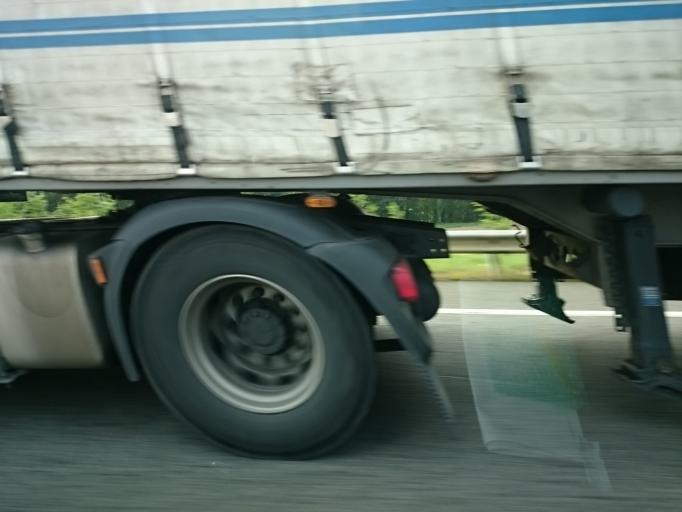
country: FR
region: Brittany
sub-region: Departement d'Ille-et-Vilaine
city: Pance
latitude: 47.8845
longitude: -1.6899
